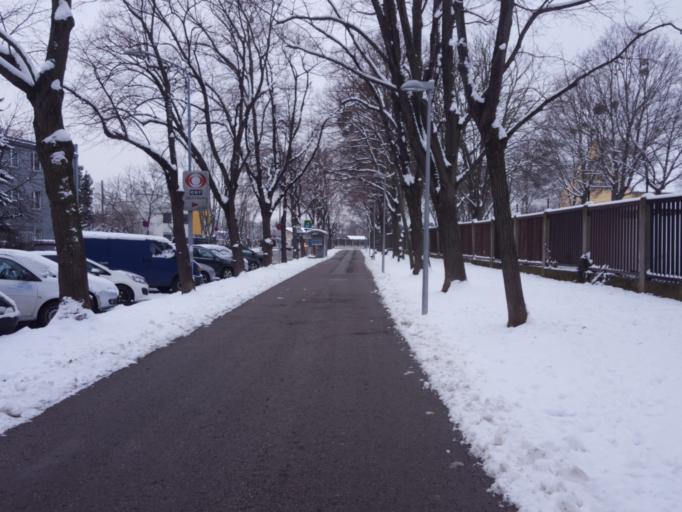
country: AT
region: Lower Austria
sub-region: Politischer Bezirk Modling
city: Vosendorf
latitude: 48.1716
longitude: 16.3092
